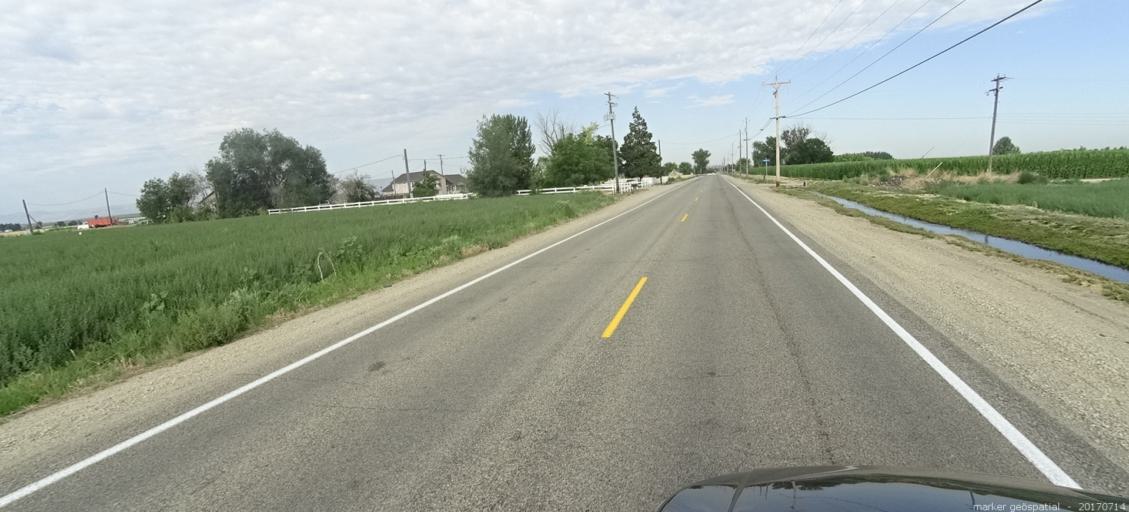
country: US
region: Idaho
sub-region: Ada County
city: Kuna
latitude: 43.4883
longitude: -116.4627
